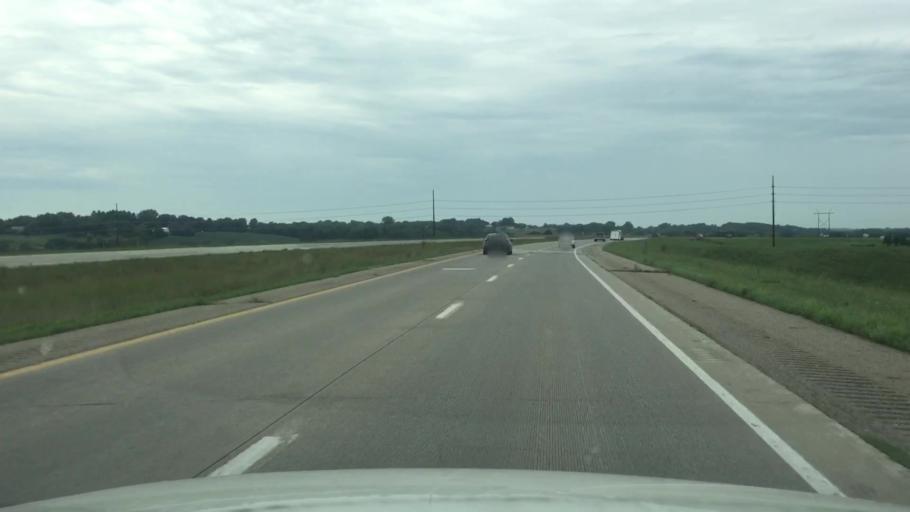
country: US
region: Iowa
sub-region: Warren County
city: Norwalk
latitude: 41.4986
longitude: -93.6220
